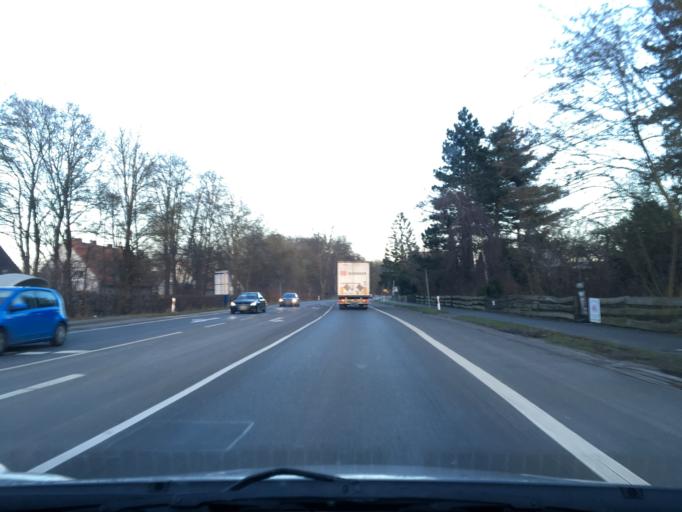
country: DE
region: Lower Saxony
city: Uelzen
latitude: 52.9705
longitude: 10.5923
